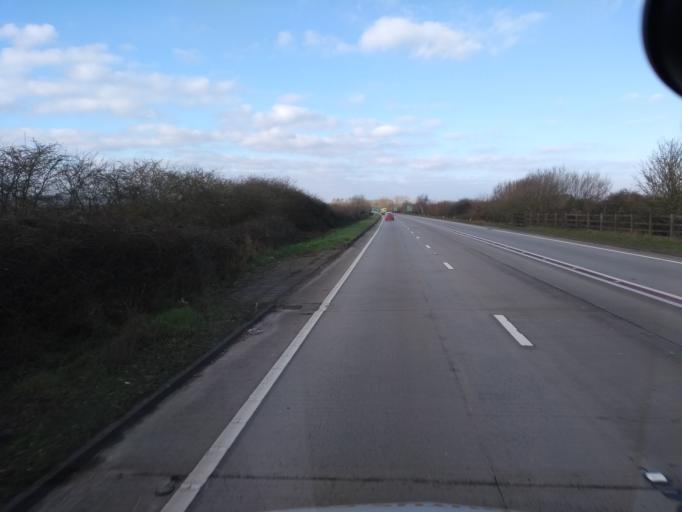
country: GB
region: England
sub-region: Somerset
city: Ilminster
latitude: 50.9417
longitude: -2.8898
